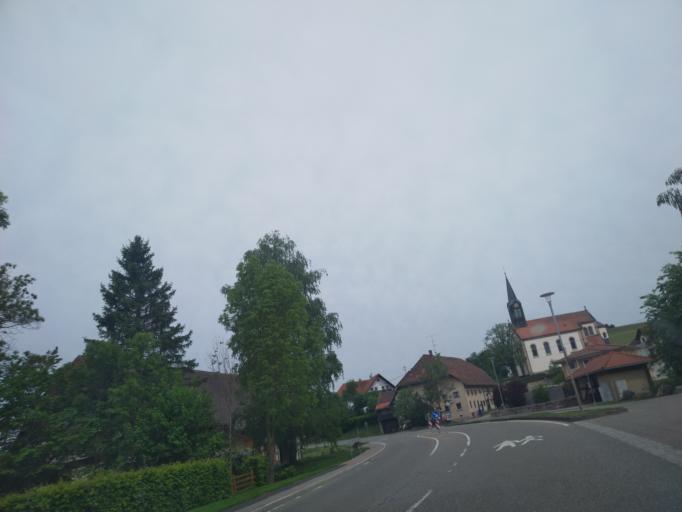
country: DE
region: Baden-Wuerttemberg
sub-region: Freiburg Region
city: Bonndorf im Schwarzwald
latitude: 47.7978
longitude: 8.3521
